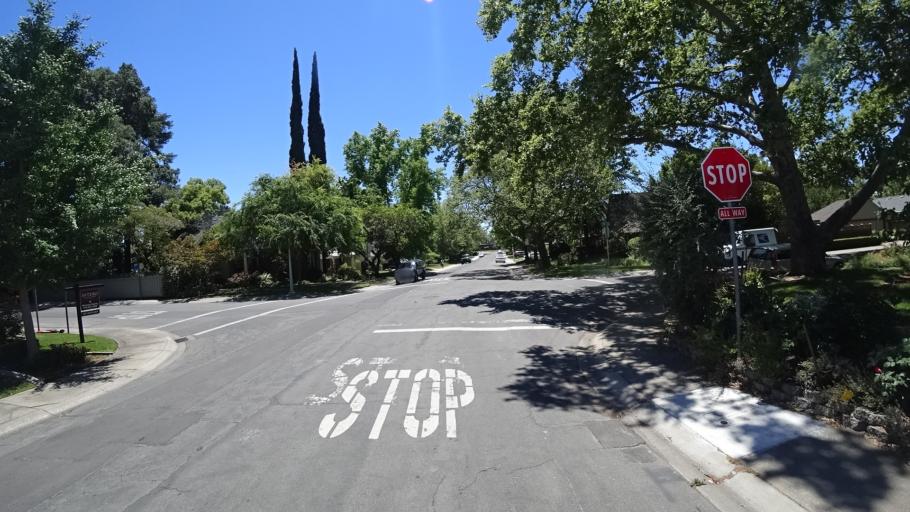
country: US
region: California
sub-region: Sacramento County
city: Sacramento
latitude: 38.5710
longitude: -121.4412
